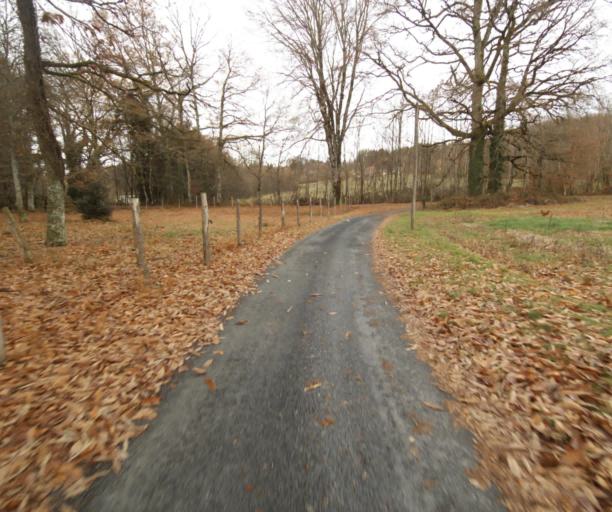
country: FR
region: Limousin
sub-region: Departement de la Correze
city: Chameyrat
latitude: 45.2664
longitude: 1.6963
